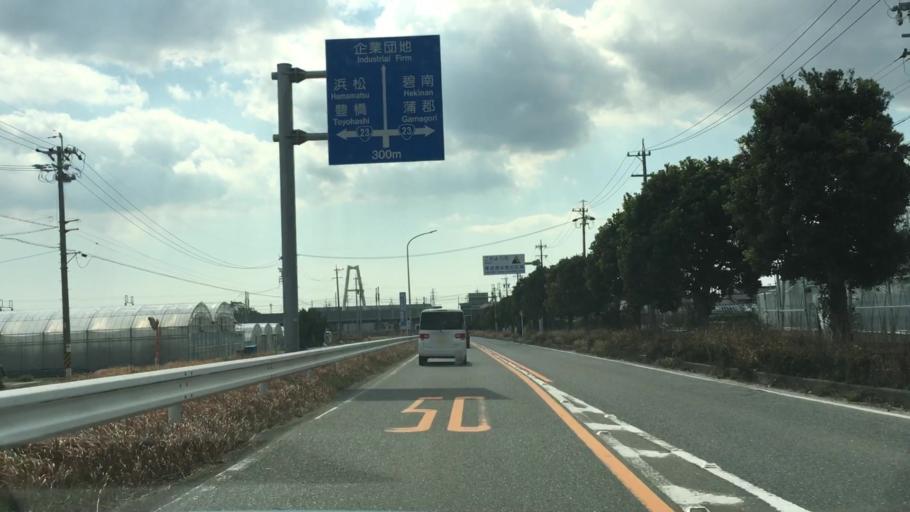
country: JP
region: Aichi
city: Kozakai-cho
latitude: 34.8109
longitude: 137.3099
